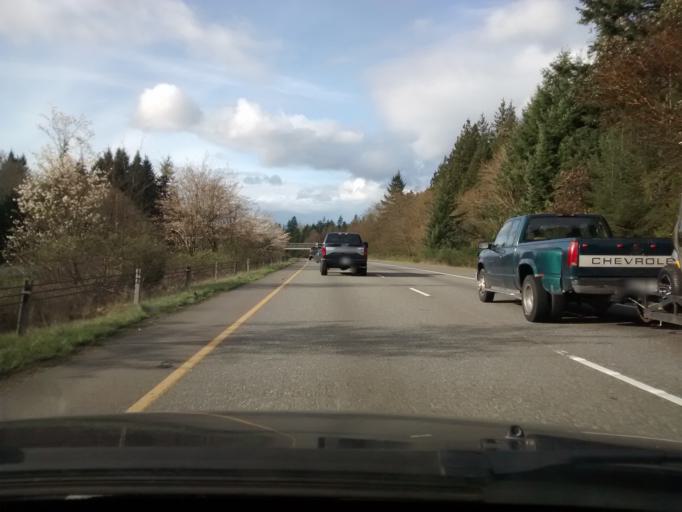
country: US
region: Washington
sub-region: Pierce County
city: Purdy
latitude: 47.3858
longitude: -122.6155
